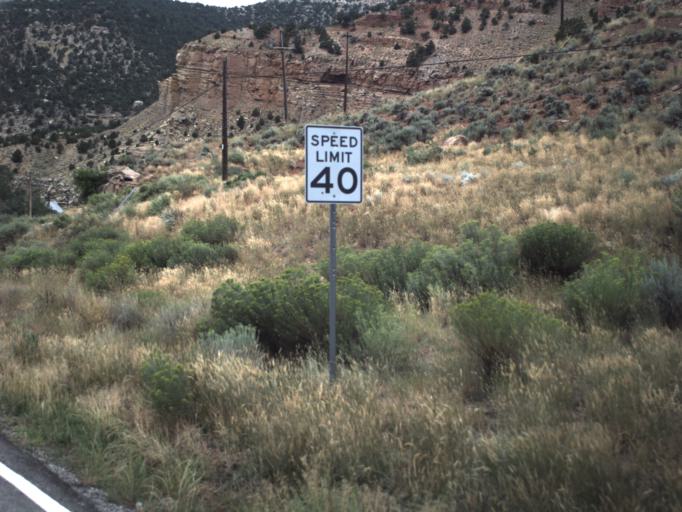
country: US
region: Utah
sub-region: Carbon County
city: East Carbon City
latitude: 39.5603
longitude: -110.3744
